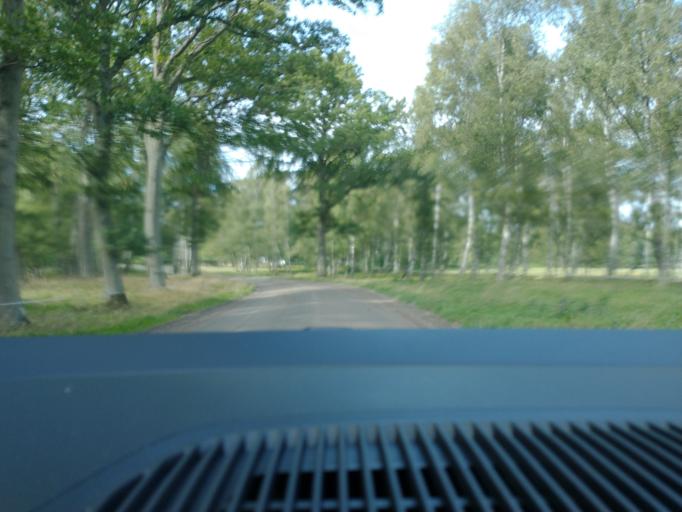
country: SE
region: Skane
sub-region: Lunds Kommun
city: Veberod
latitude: 55.6717
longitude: 13.4523
